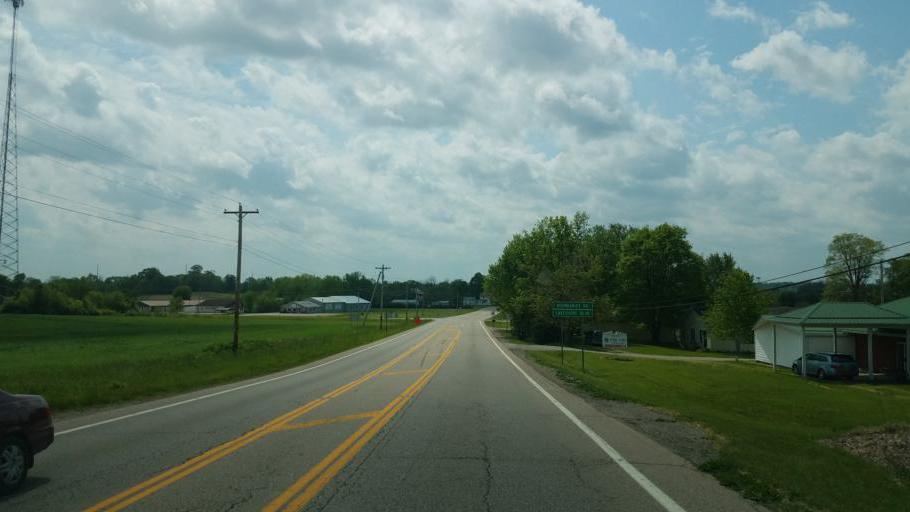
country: US
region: Ohio
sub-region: Perry County
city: Thornport
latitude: 39.9242
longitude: -82.4097
